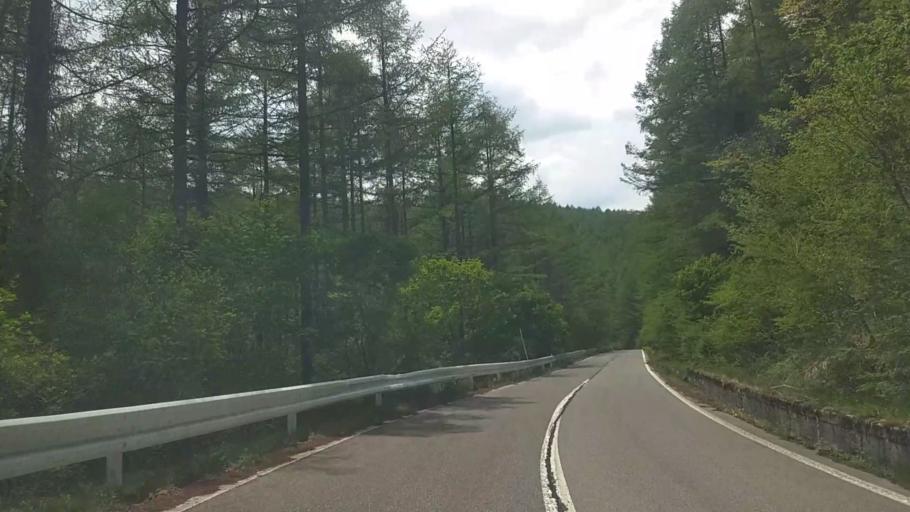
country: JP
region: Nagano
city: Saku
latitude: 36.0924
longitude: 138.3872
